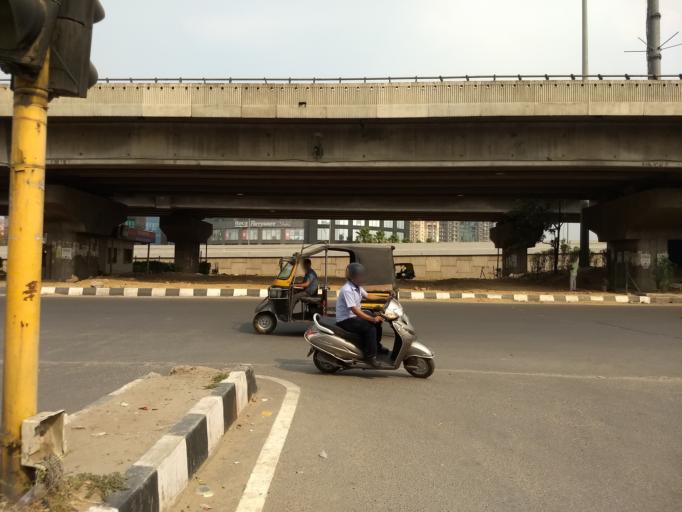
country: IN
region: Haryana
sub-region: Gurgaon
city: Gurgaon
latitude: 28.4794
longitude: 77.0702
